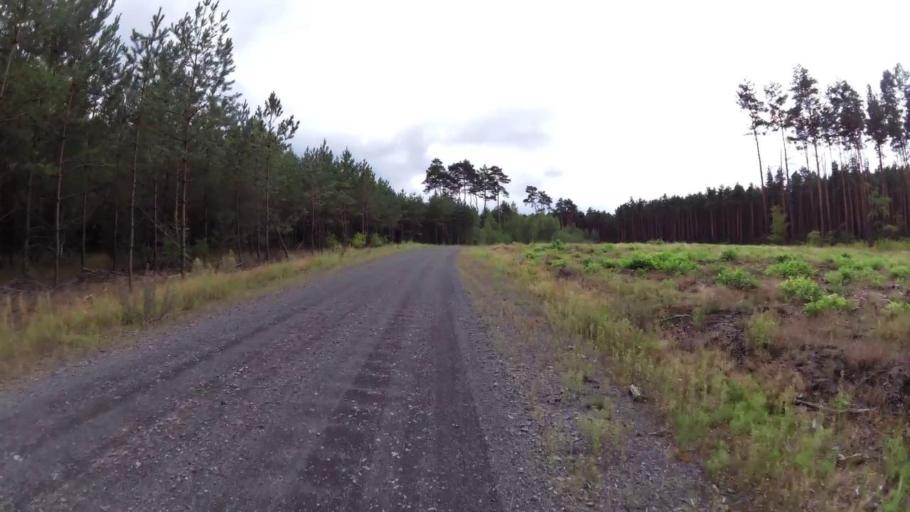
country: PL
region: West Pomeranian Voivodeship
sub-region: Powiat mysliborski
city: Debno
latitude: 52.7786
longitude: 14.7211
